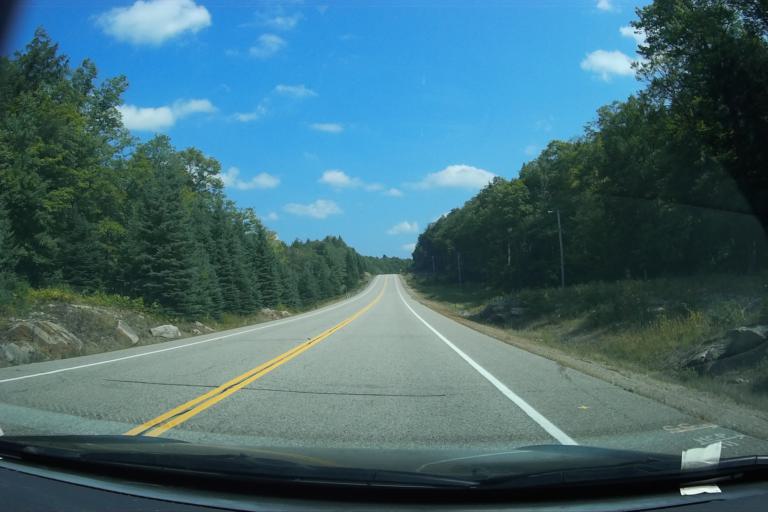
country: CA
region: Ontario
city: Huntsville
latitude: 45.5637
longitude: -78.5687
